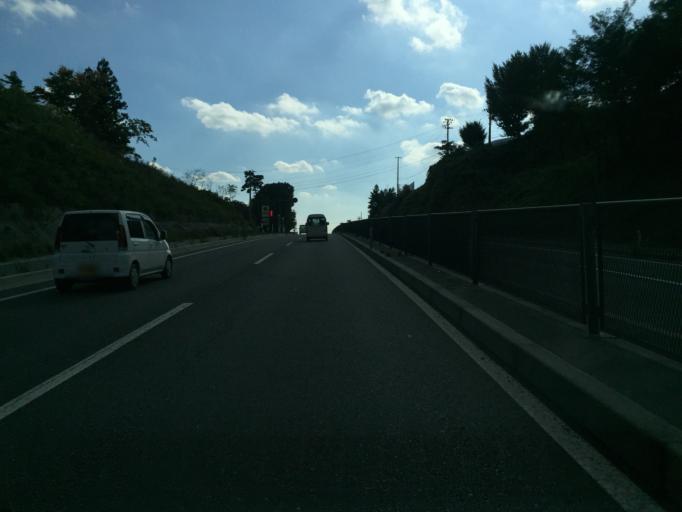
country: JP
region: Fukushima
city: Motomiya
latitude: 37.5525
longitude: 140.4018
